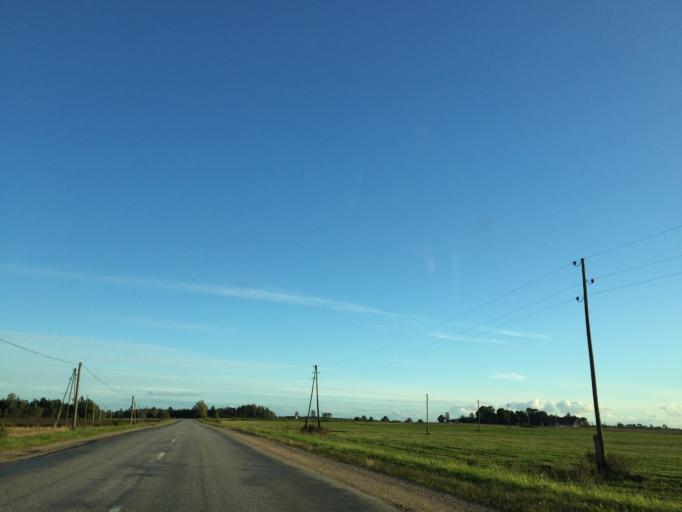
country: LV
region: Saldus Rajons
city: Saldus
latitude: 56.7396
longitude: 22.3774
